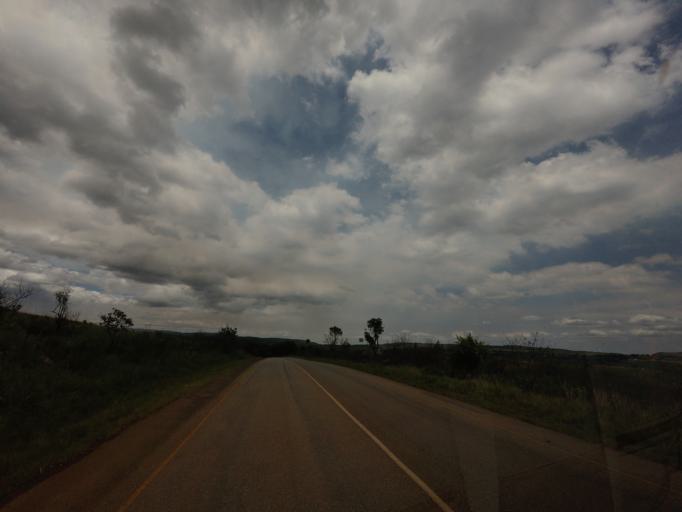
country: ZA
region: Mpumalanga
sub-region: Ehlanzeni District
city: Graksop
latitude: -24.9251
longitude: 30.8128
